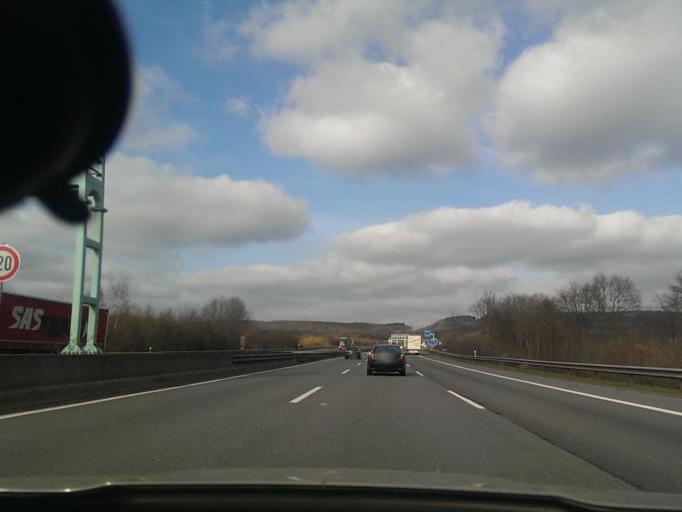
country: DE
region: North Rhine-Westphalia
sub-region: Regierungsbezirk Detmold
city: Herford
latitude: 52.0942
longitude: 8.7035
